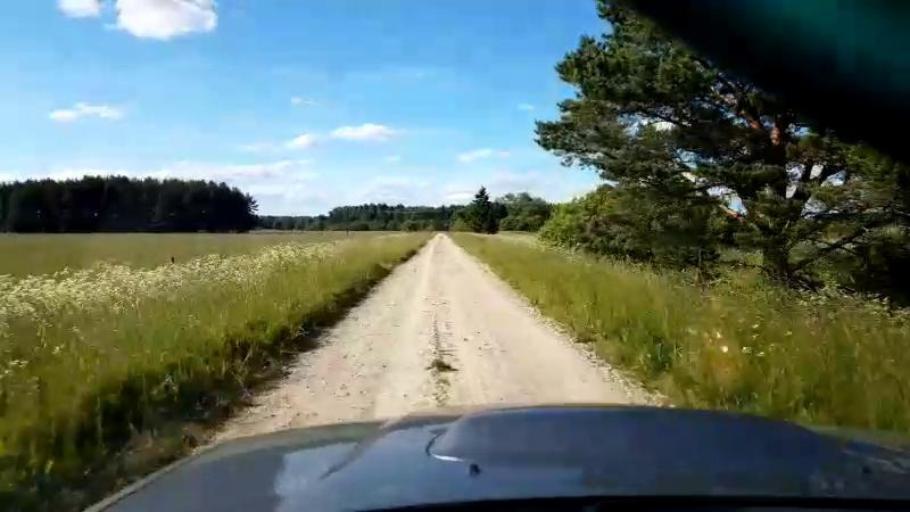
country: EE
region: Paernumaa
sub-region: Sauga vald
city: Sauga
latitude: 58.5082
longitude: 24.5900
